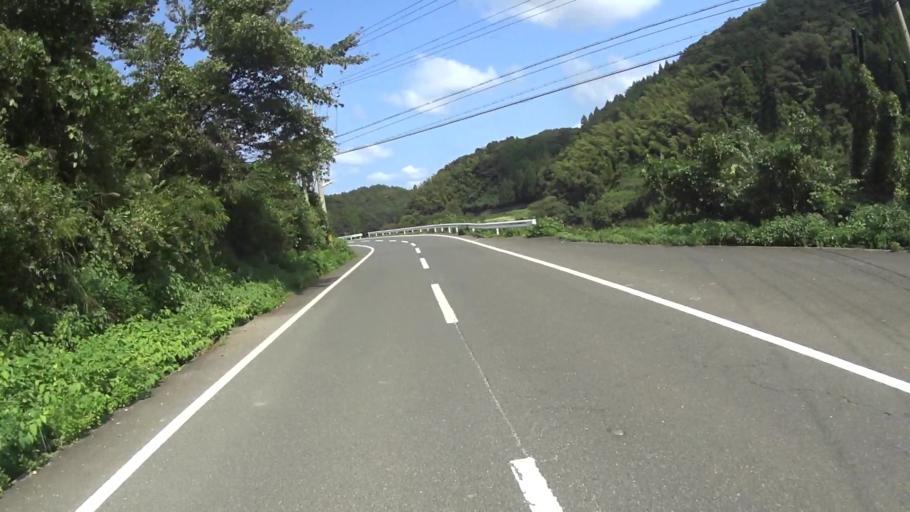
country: JP
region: Kyoto
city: Miyazu
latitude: 35.6996
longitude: 135.2498
